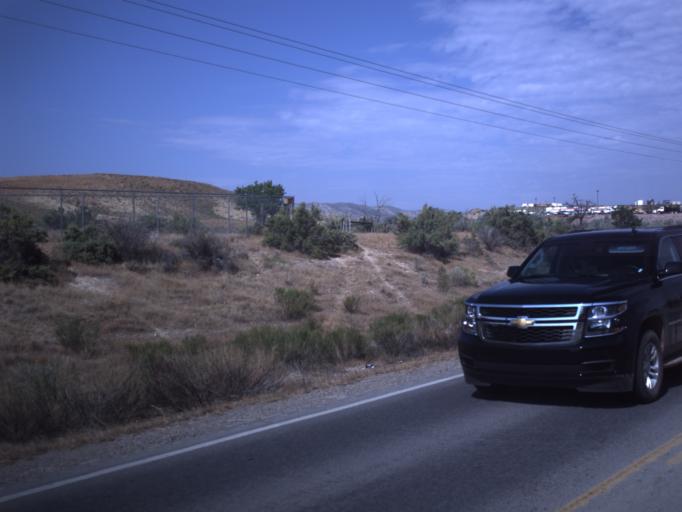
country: US
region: Utah
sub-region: Uintah County
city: Naples
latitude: 40.3908
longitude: -109.4444
